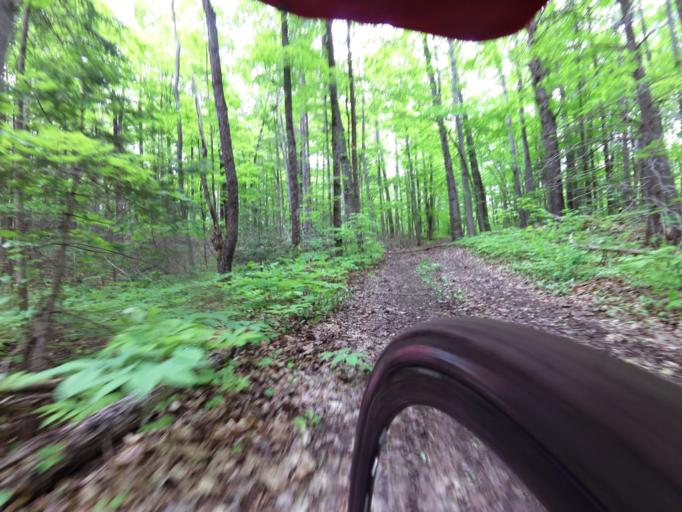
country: CA
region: Ontario
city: Arnprior
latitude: 45.1875
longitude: -76.5321
